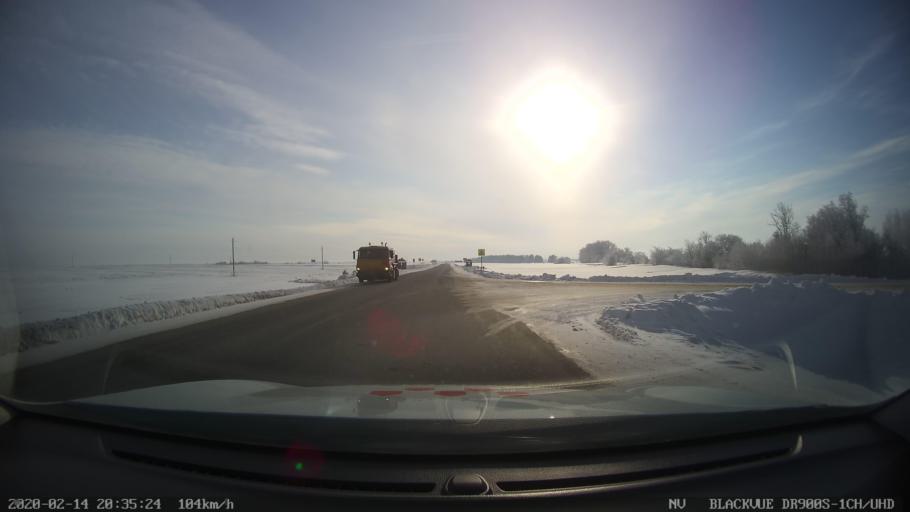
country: RU
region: Tatarstan
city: Kuybyshevskiy Zaton
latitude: 55.3827
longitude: 48.9832
